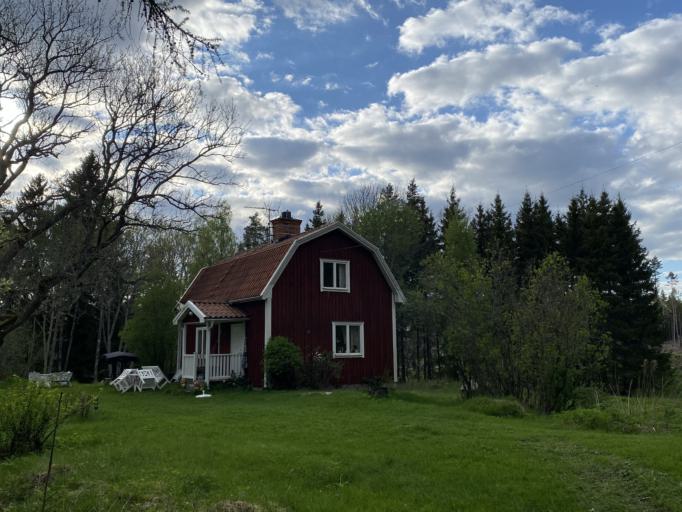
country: SE
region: Soedermanland
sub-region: Flens Kommun
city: Halleforsnas
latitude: 59.1789
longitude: 16.5233
